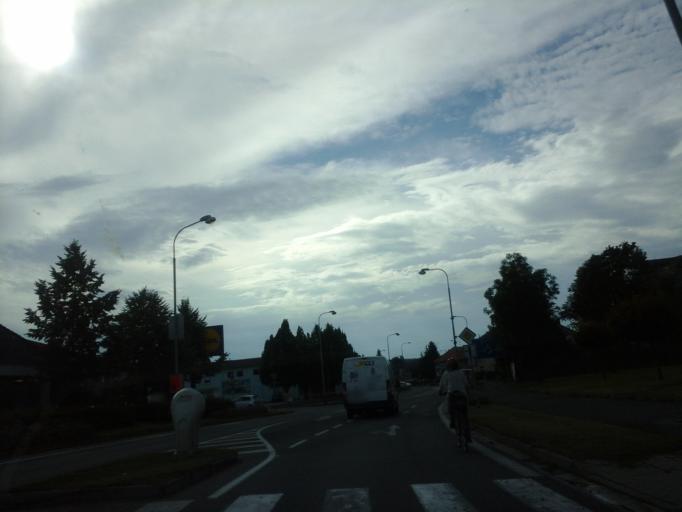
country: CZ
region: Pardubicky
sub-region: Okres Usti nad Orlici
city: Lanskroun
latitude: 49.9095
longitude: 16.6106
